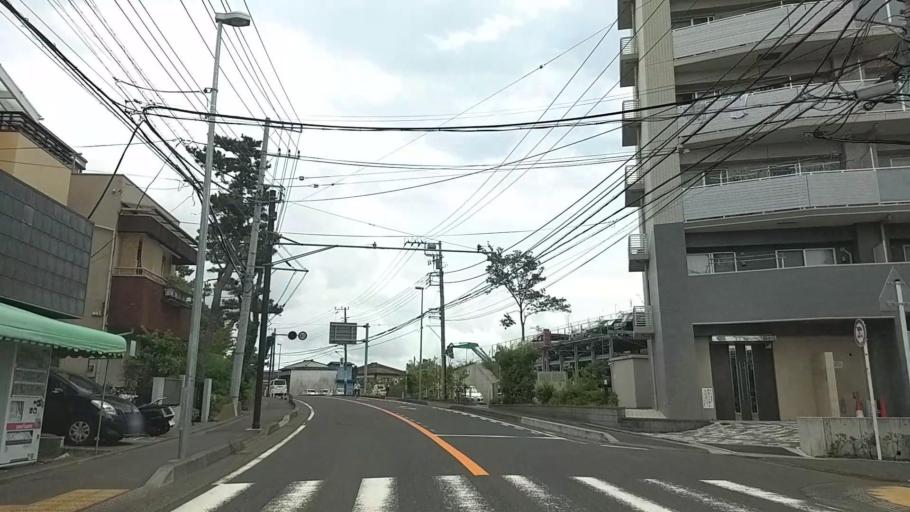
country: JP
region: Kanagawa
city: Fujisawa
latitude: 35.3461
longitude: 139.4515
